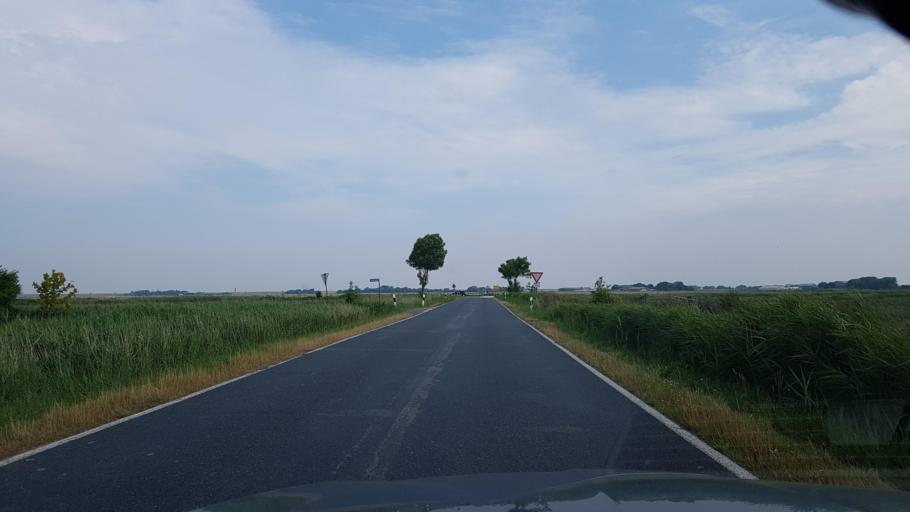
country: DE
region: Schleswig-Holstein
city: Westerhever
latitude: 54.3782
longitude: 8.6900
